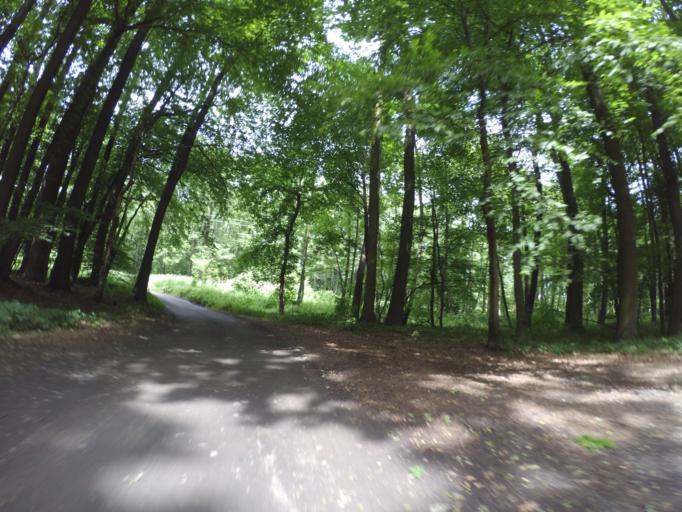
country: CZ
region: Central Bohemia
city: Celakovice
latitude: 50.1799
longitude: 14.7853
